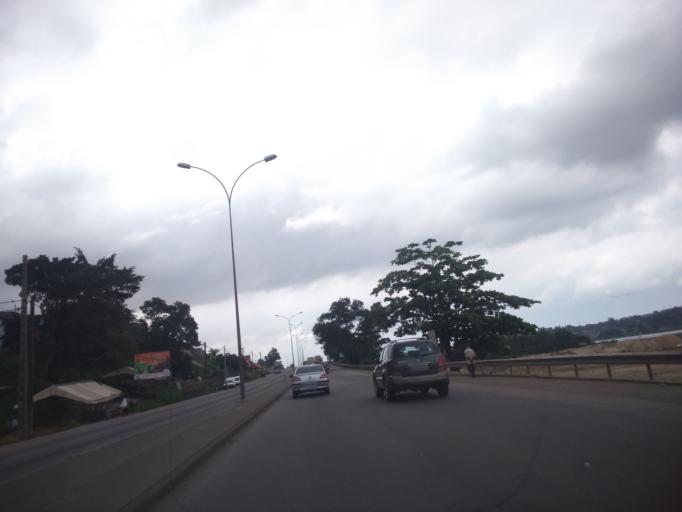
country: CI
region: Lagunes
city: Abidjan
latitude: 5.3512
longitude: -4.0401
